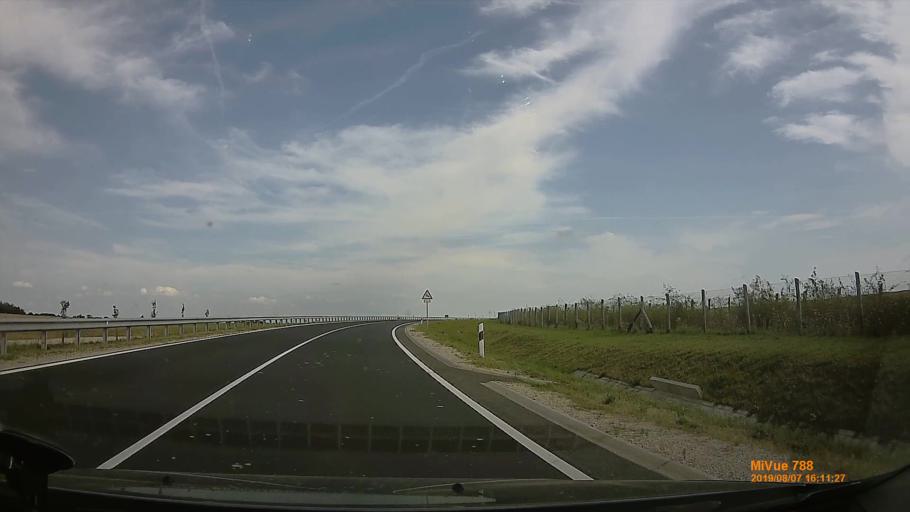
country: HU
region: Zala
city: Zalalovo
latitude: 46.8708
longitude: 16.6226
